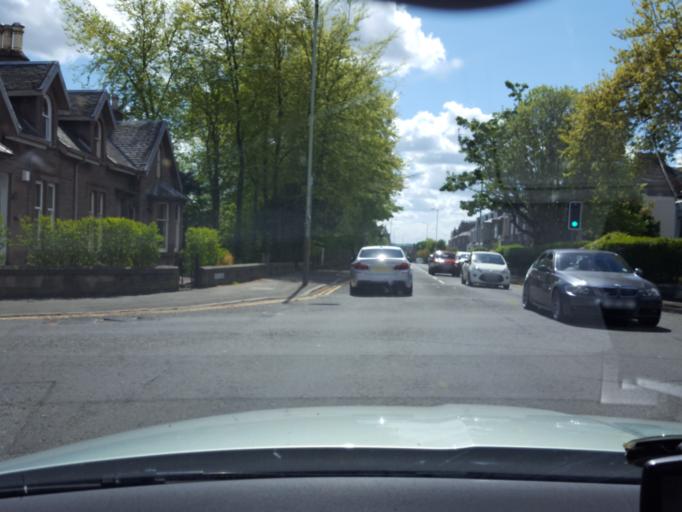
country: GB
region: Scotland
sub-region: Dundee City
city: Dundee
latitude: 56.4778
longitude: -2.9531
